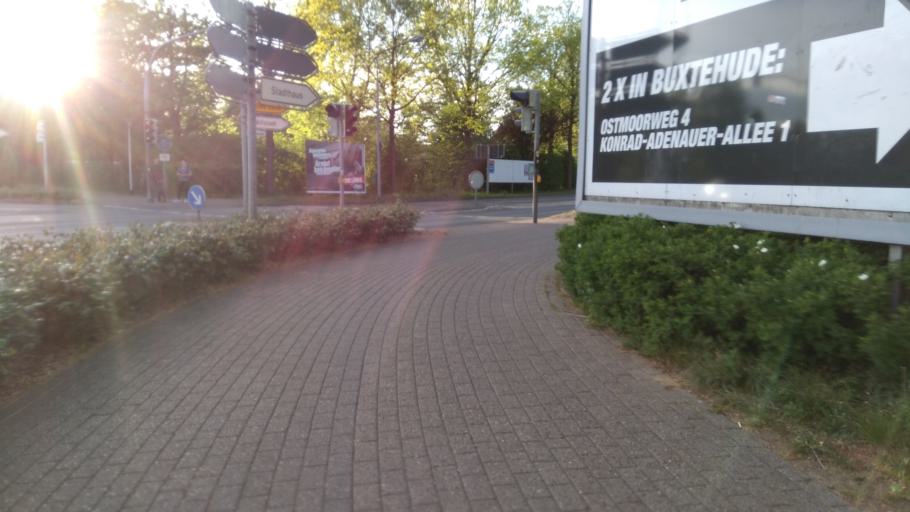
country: DE
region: Lower Saxony
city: Buxtehude
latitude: 53.4703
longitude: 9.6975
